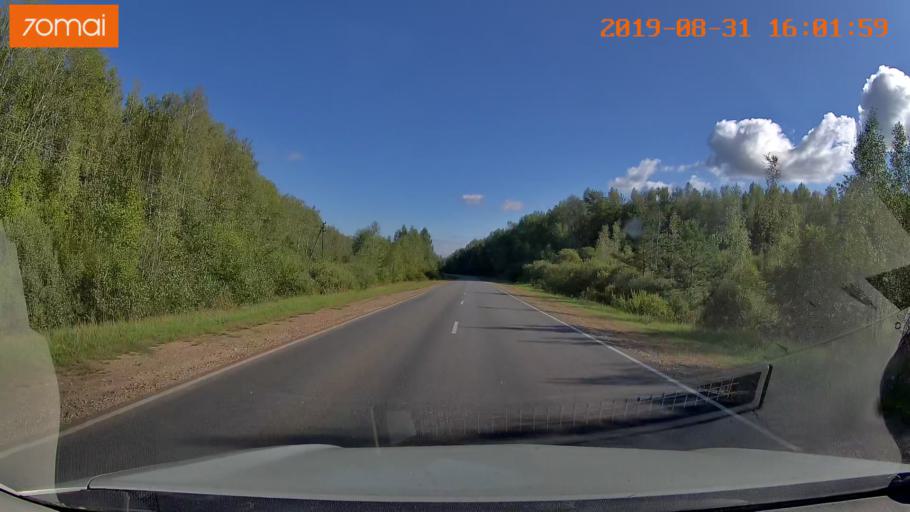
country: RU
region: Kaluga
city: Yukhnov
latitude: 54.6813
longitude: 35.2960
